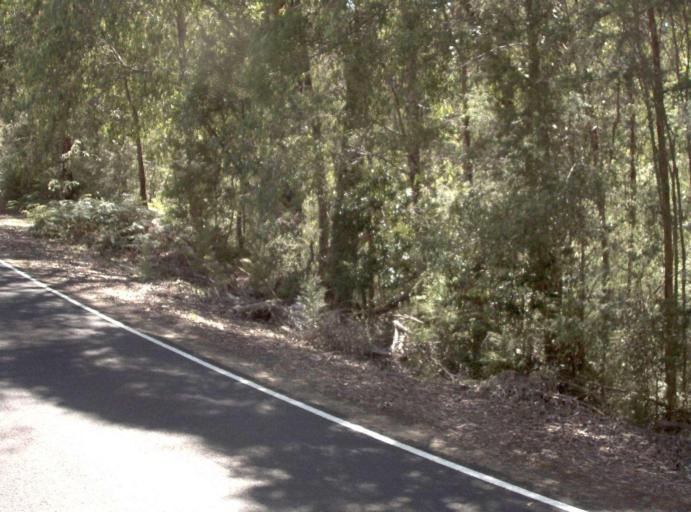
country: AU
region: Victoria
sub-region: East Gippsland
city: Lakes Entrance
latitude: -37.3662
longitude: 148.2183
